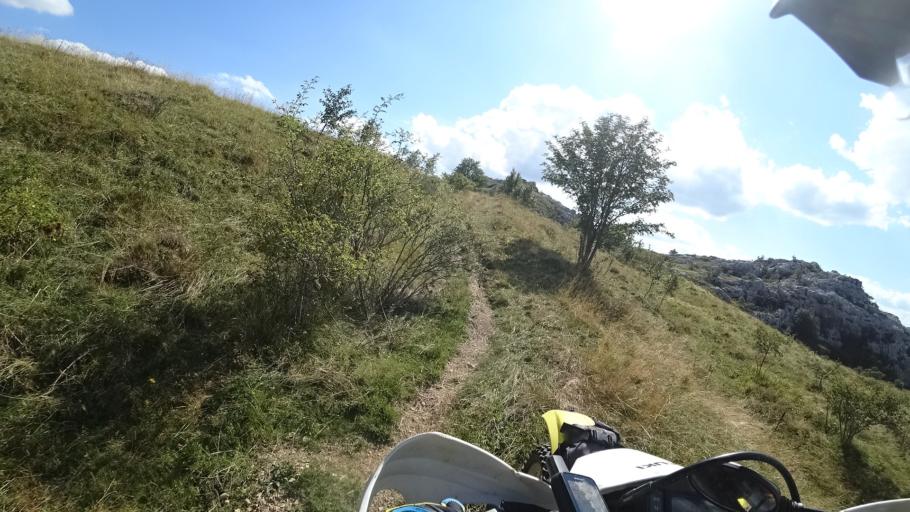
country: HR
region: Zadarska
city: Gracac
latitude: 44.4082
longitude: 16.0030
